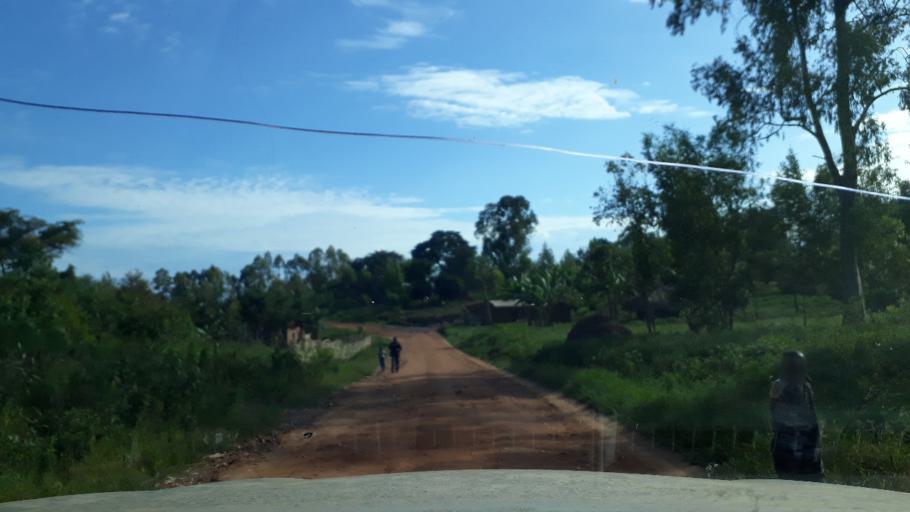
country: UG
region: Northern Region
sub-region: Zombo District
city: Paidha
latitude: 2.3316
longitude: 31.0266
